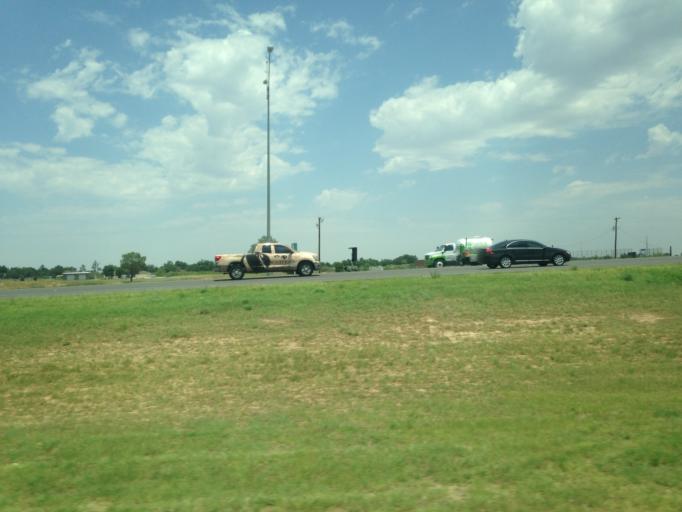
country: US
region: Texas
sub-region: Midland County
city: Midland
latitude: 32.0427
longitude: -102.0888
